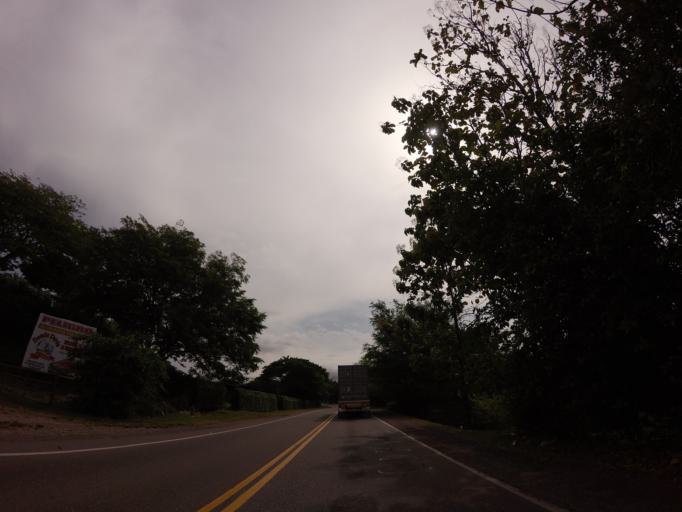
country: CO
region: Caldas
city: La Dorada
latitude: 5.4233
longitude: -74.6836
